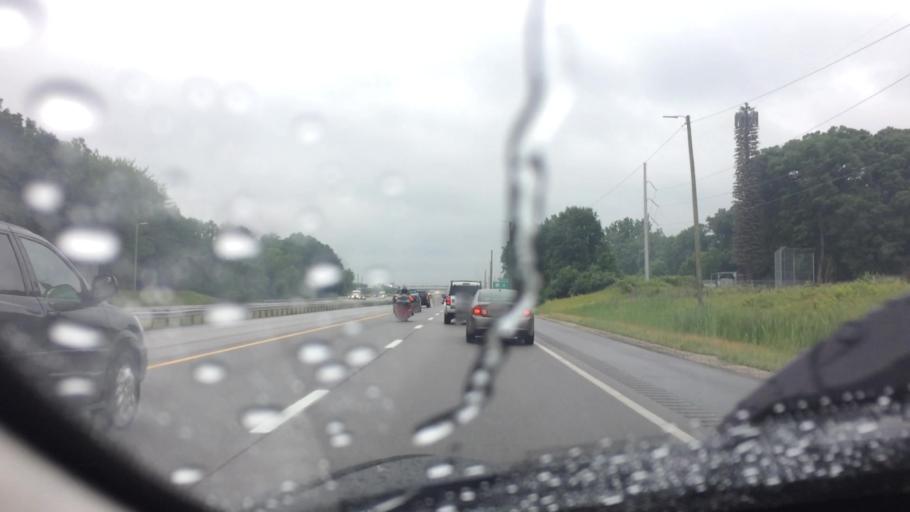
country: US
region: Ohio
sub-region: Lucas County
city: Holland
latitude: 41.6046
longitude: -83.6911
